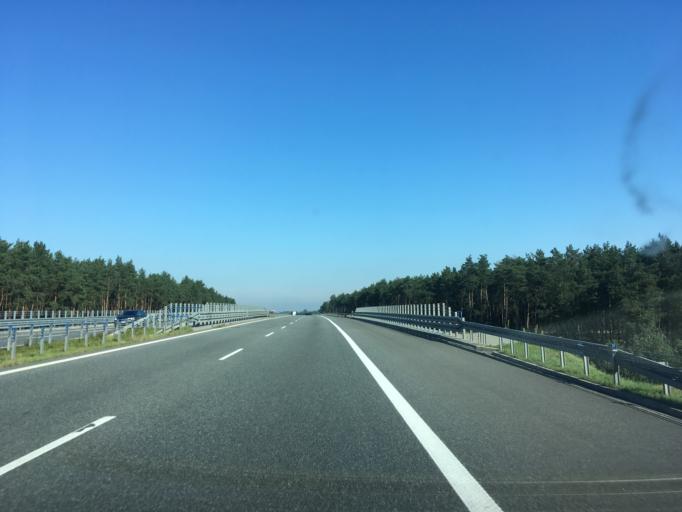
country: PL
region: Kujawsko-Pomorskie
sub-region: Powiat torunski
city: Lubicz Dolny
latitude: 53.1515
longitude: 18.7453
